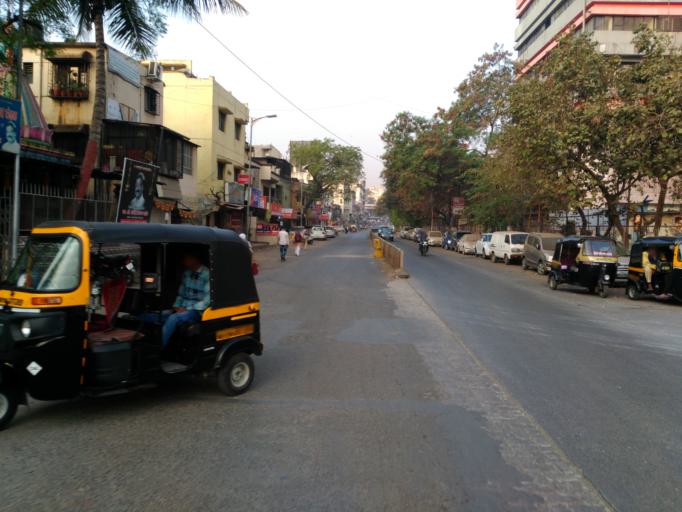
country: IN
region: Maharashtra
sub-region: Pune Division
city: Pune
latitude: 18.4689
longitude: 73.8608
